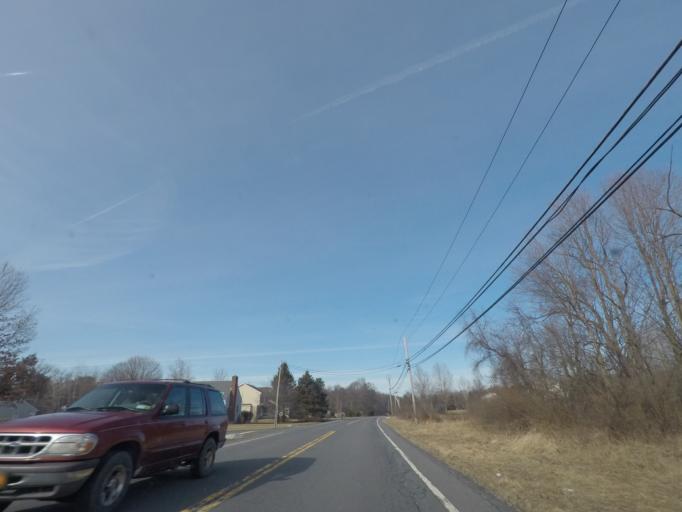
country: US
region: New York
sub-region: Rensselaer County
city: Nassau
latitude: 42.4871
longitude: -73.6248
